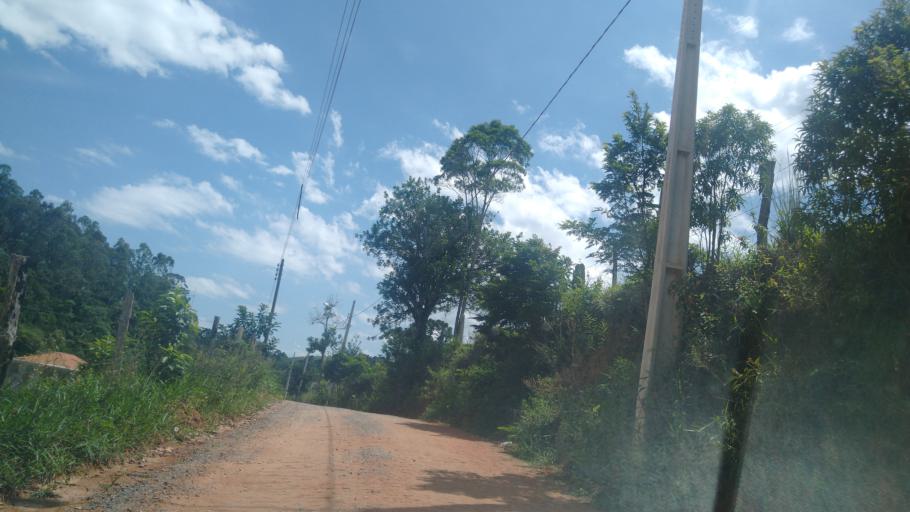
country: BR
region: Minas Gerais
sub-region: Extrema
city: Extrema
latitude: -22.7450
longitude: -46.2987
